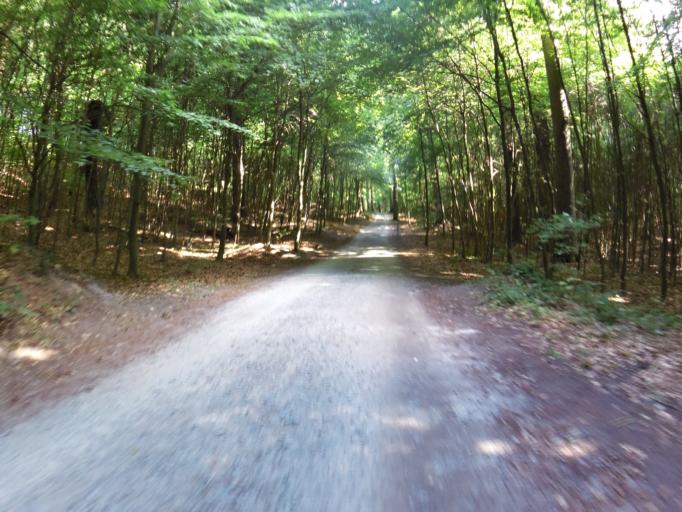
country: DE
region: Mecklenburg-Vorpommern
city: Koserow
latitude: 54.0527
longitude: 14.0109
